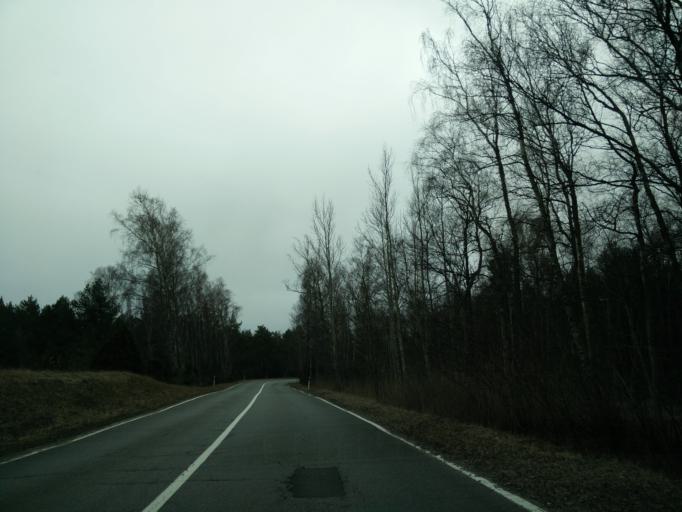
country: LT
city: Neringa
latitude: 55.4445
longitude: 21.0722
